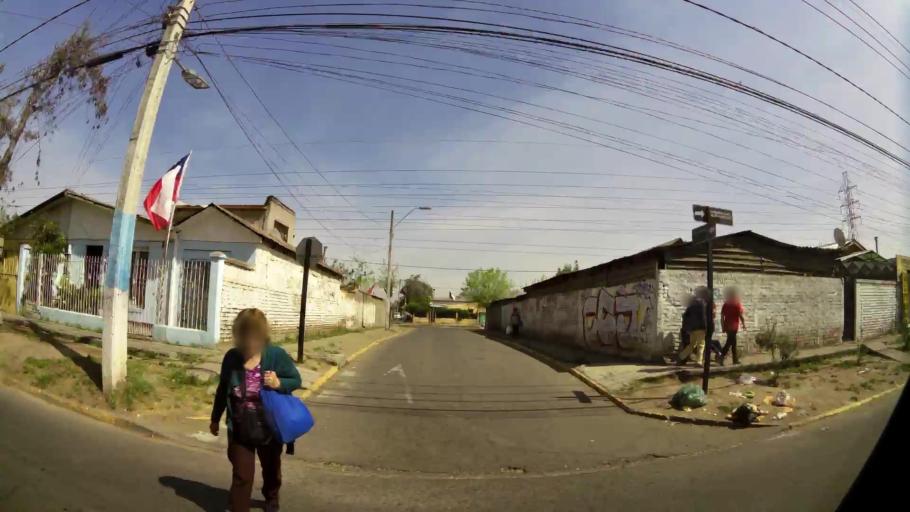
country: CL
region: Santiago Metropolitan
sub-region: Provincia de Santiago
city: Lo Prado
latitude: -33.4348
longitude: -70.7303
